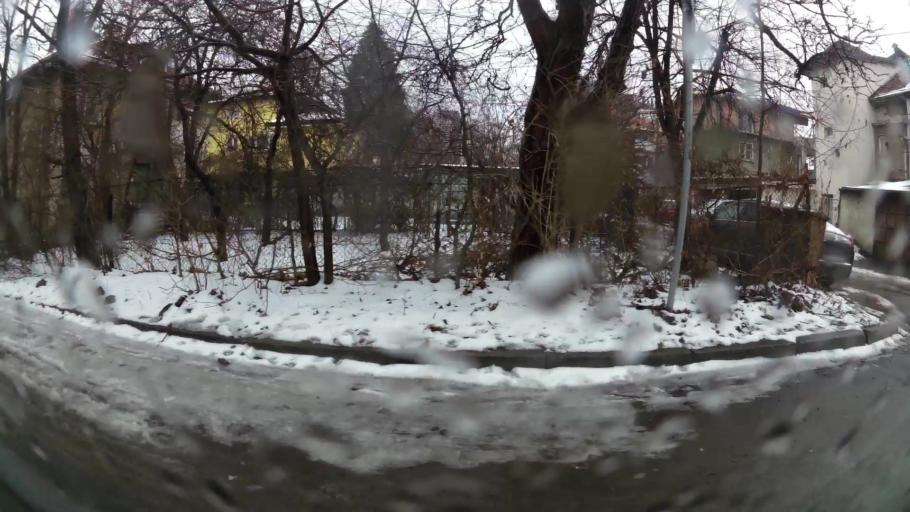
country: BG
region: Sofia-Capital
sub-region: Stolichna Obshtina
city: Sofia
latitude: 42.6657
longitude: 23.2771
